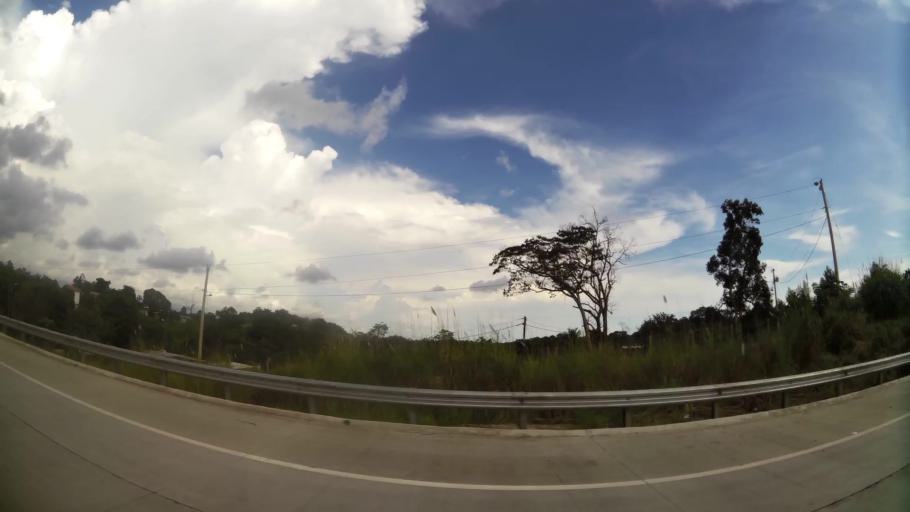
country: PA
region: Panama
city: Tocumen
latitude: 9.0956
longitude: -79.4218
